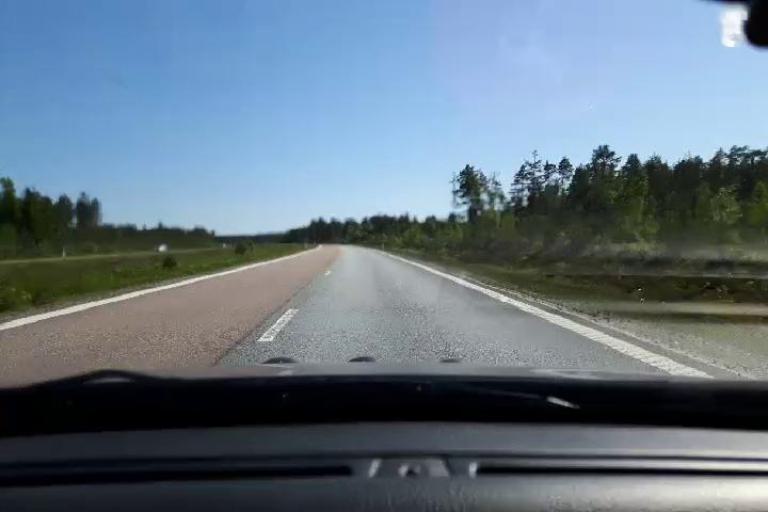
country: SE
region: Gaevleborg
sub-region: Soderhamns Kommun
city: Soderhamn
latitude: 61.3875
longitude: 16.9917
